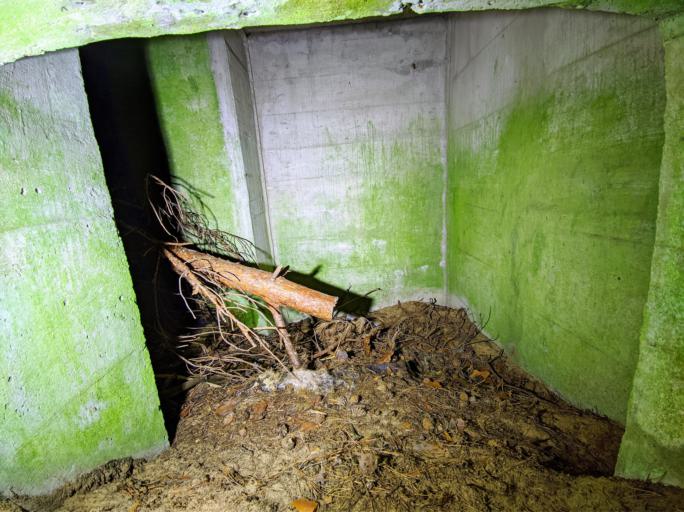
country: PL
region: Lubusz
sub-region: Powiat swiebodzinski
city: Miedzylesie
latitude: 52.0966
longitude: 15.4005
